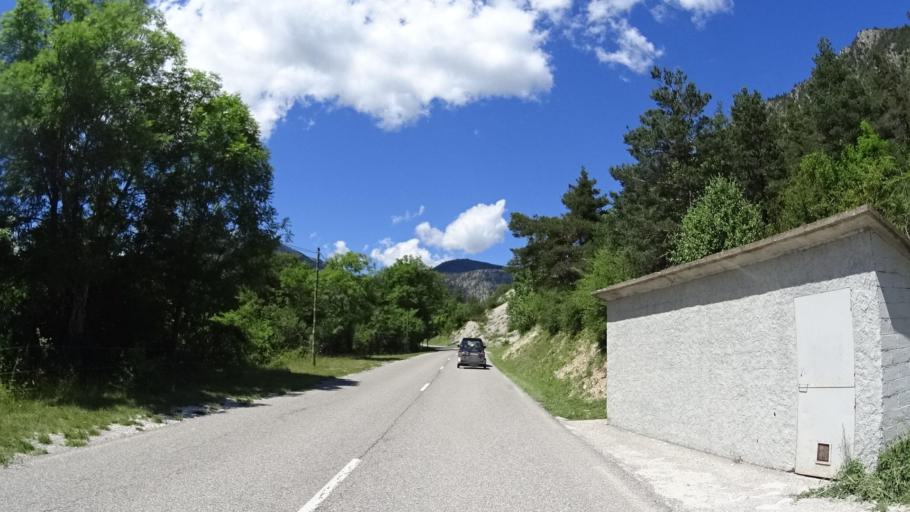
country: FR
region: Provence-Alpes-Cote d'Azur
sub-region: Departement des Alpes-de-Haute-Provence
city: Annot
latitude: 44.0808
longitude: 6.5682
